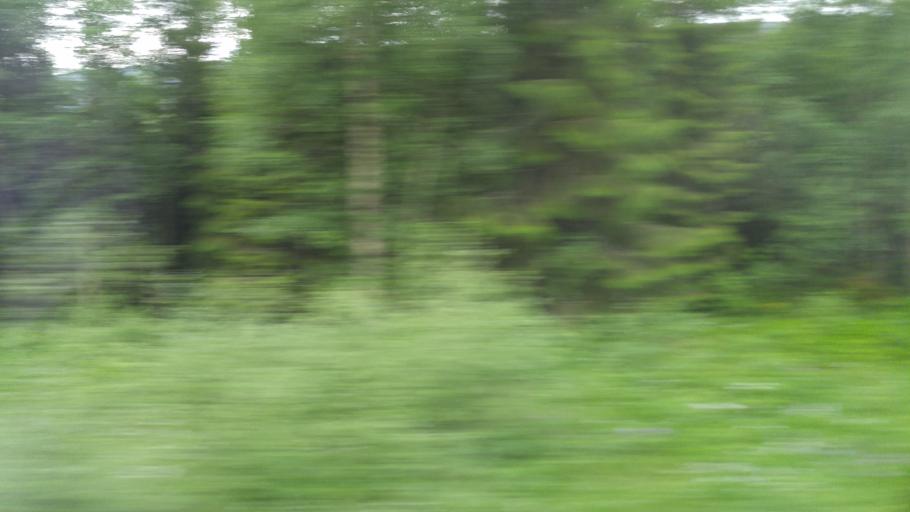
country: NO
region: Nord-Trondelag
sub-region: Meraker
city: Meraker
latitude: 63.4004
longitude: 11.7963
